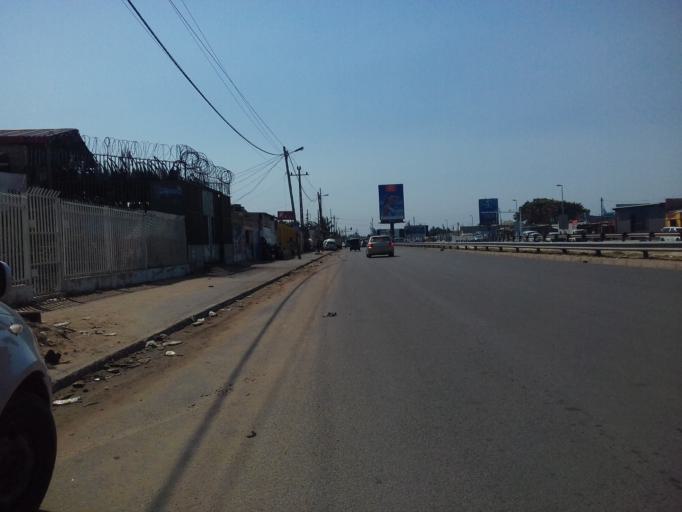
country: MZ
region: Maputo City
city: Maputo
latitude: -25.9481
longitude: 32.5801
